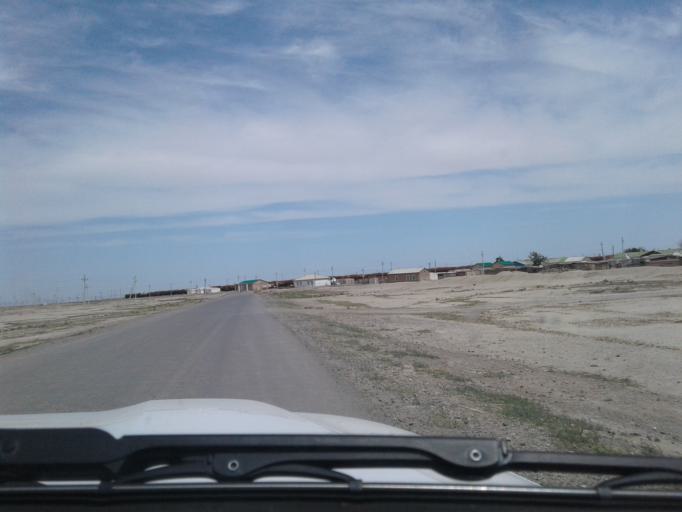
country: TM
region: Balkan
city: Gazanjyk
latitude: 39.2090
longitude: 55.7093
